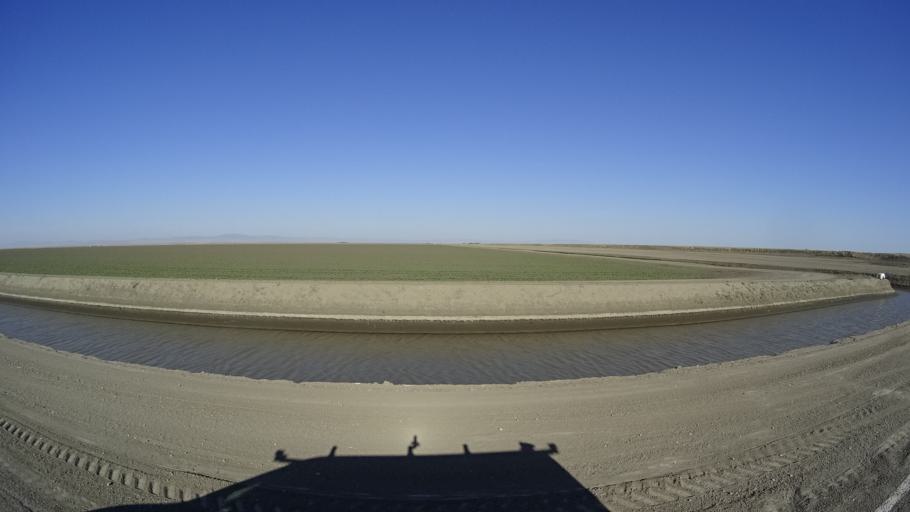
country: US
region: California
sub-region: Kings County
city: Stratford
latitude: 36.1369
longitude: -119.7981
